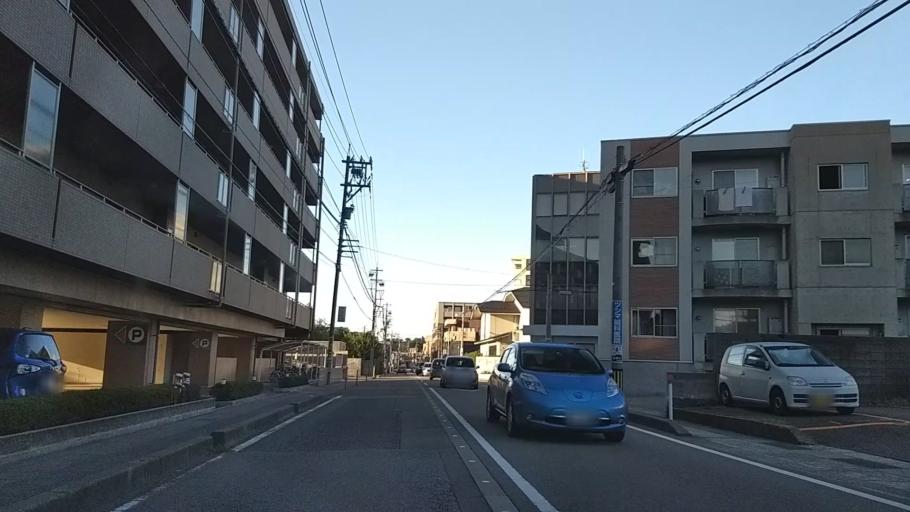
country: JP
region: Ishikawa
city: Nonoichi
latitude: 36.5454
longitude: 136.6490
